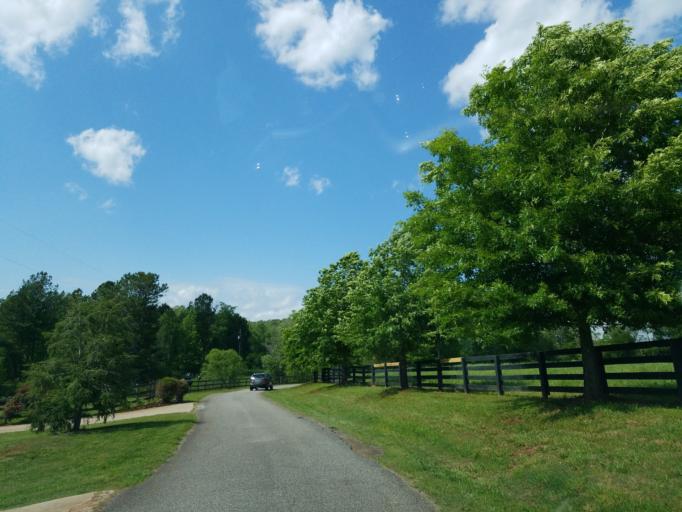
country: US
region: Georgia
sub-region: Cherokee County
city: Ball Ground
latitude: 34.2787
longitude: -84.3121
